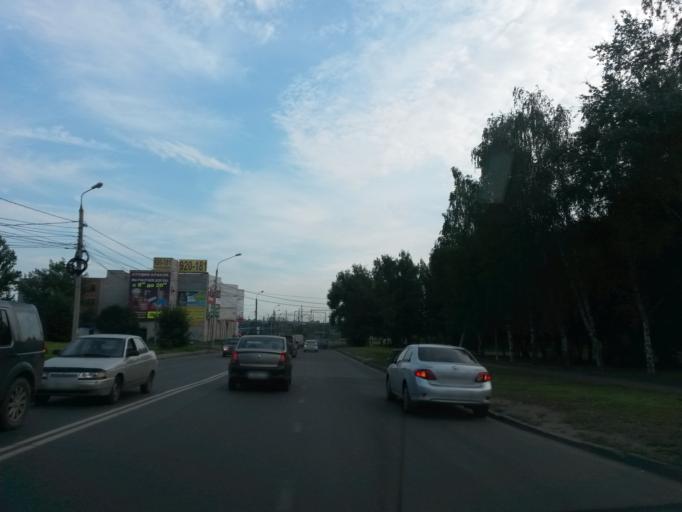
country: RU
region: Jaroslavl
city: Yaroslavl
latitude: 57.6204
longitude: 39.8484
